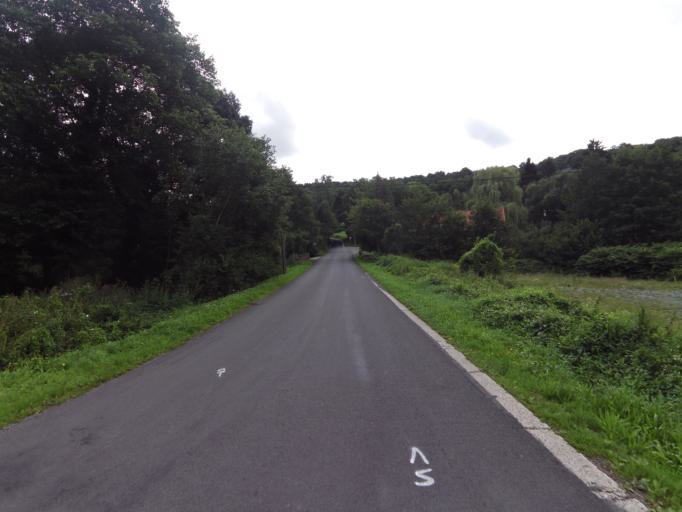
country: BE
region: Wallonia
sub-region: Province de Liege
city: Amay
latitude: 50.5372
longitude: 5.3506
